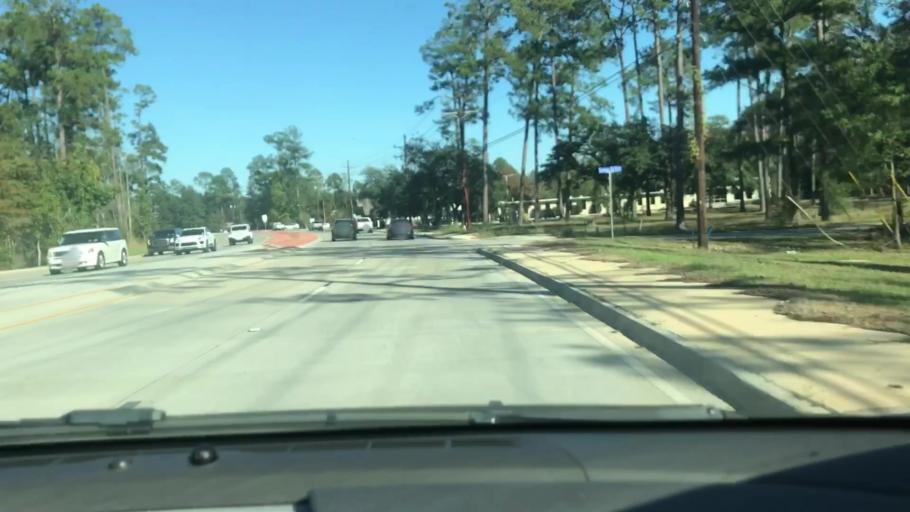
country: US
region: Louisiana
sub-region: Saint Tammany Parish
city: Covington
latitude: 30.4593
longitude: -90.1231
